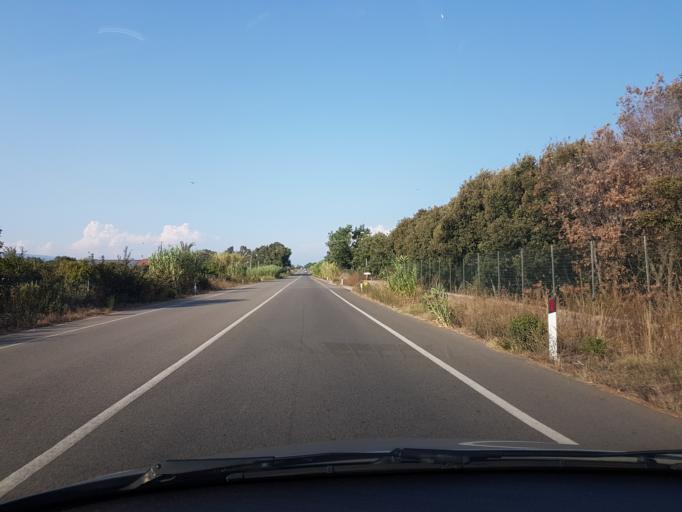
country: IT
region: Sardinia
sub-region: Provincia di Oristano
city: Nuraxinieddu
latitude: 39.9528
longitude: 8.6102
